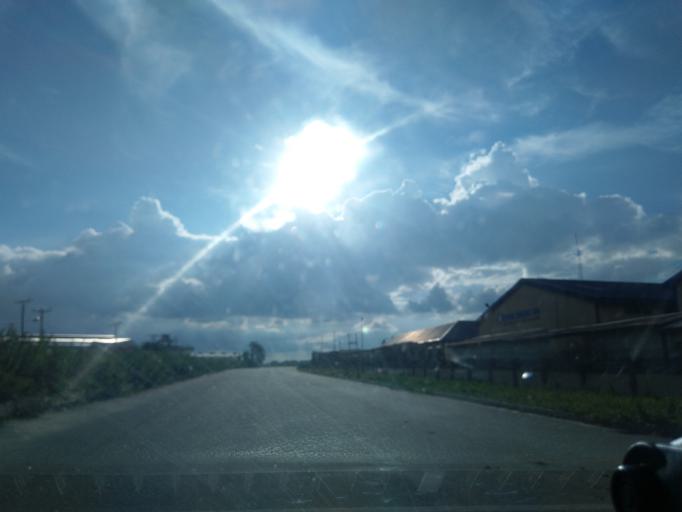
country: NG
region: Abuja Federal Capital Territory
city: Abuja
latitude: 9.0298
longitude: 7.4019
